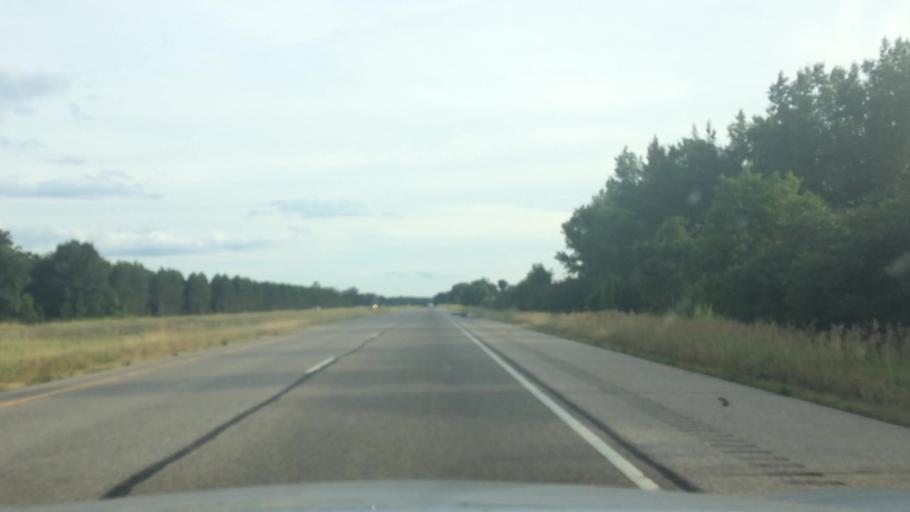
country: US
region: Wisconsin
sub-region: Waushara County
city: Wautoma
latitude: 44.1826
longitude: -89.5279
